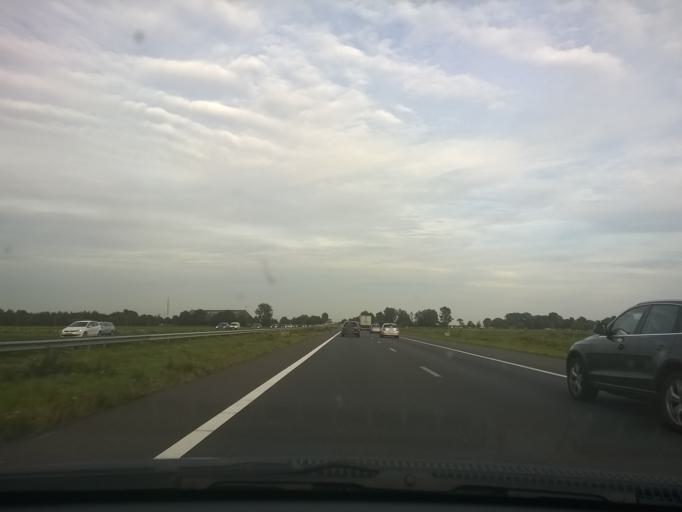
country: NL
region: Groningen
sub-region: Gemeente Zuidhorn
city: Zuidhorn
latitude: 53.1957
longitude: 6.4380
